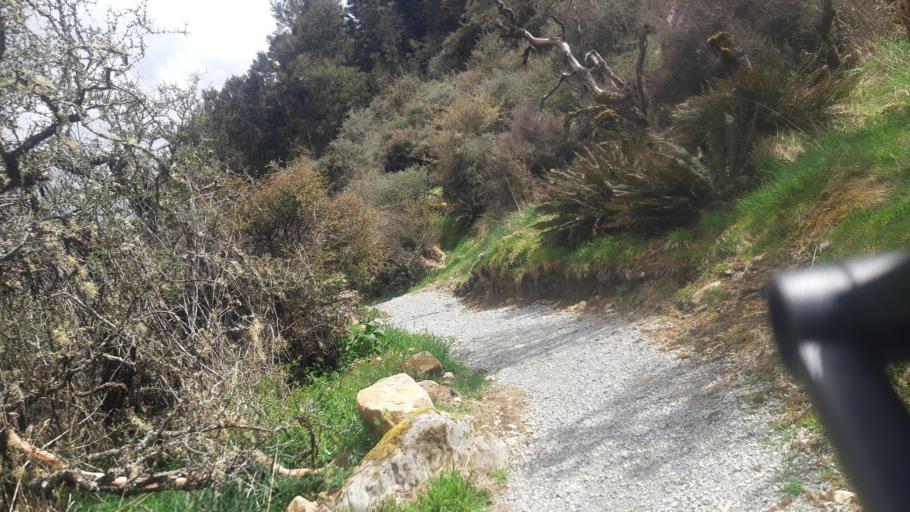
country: NZ
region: Tasman
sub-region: Tasman District
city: Wakefield
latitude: -41.7924
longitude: 172.8314
